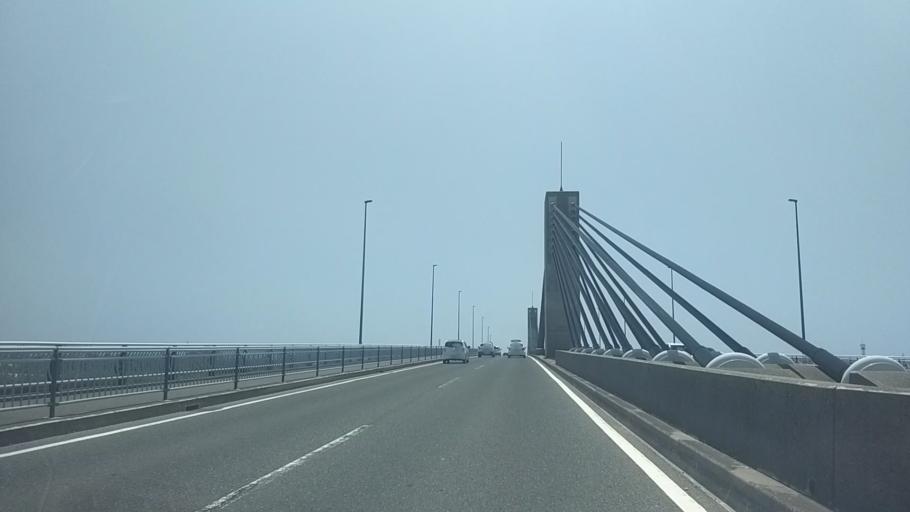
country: JP
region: Shizuoka
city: Hamamatsu
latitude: 34.6933
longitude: 137.6476
